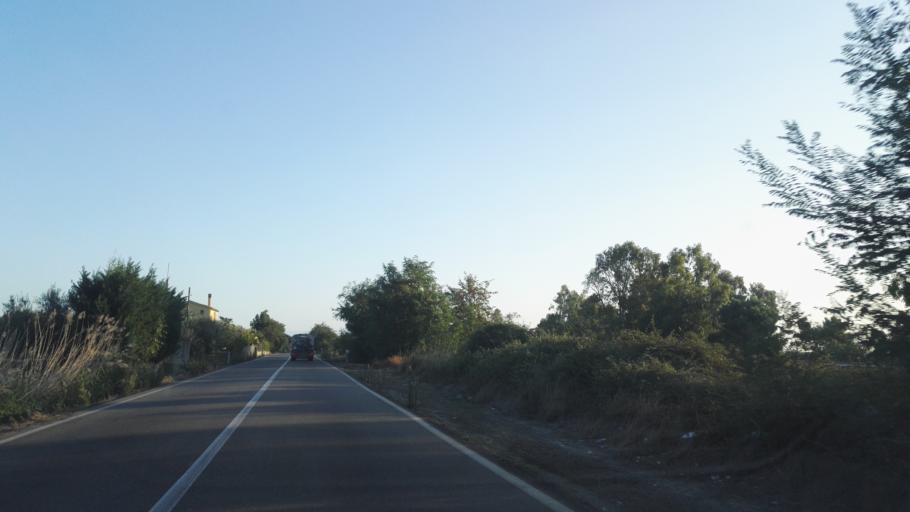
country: IT
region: Calabria
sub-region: Provincia di Catanzaro
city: Badolato Marina
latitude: 38.5520
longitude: 16.5704
